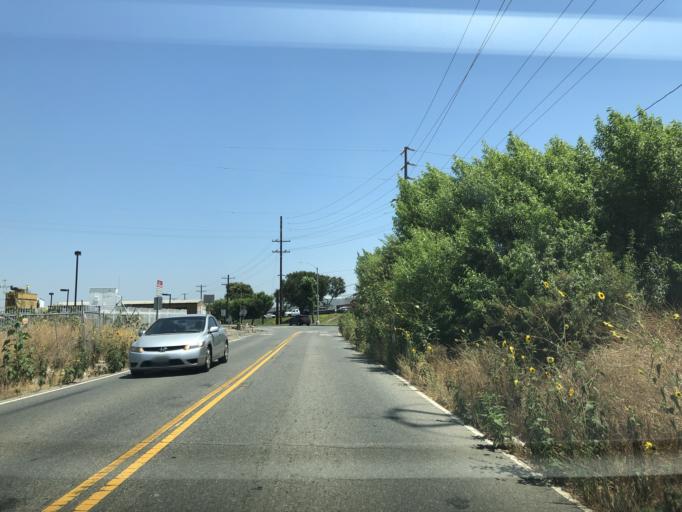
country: US
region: California
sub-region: Riverside County
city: Corona
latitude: 33.8970
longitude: -117.5903
